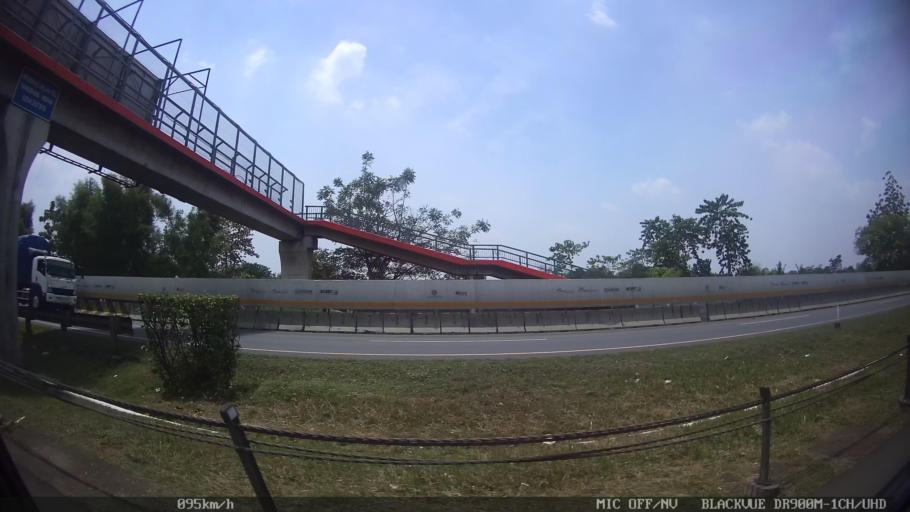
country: ID
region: Banten
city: Serang
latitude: -6.1371
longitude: 106.2178
